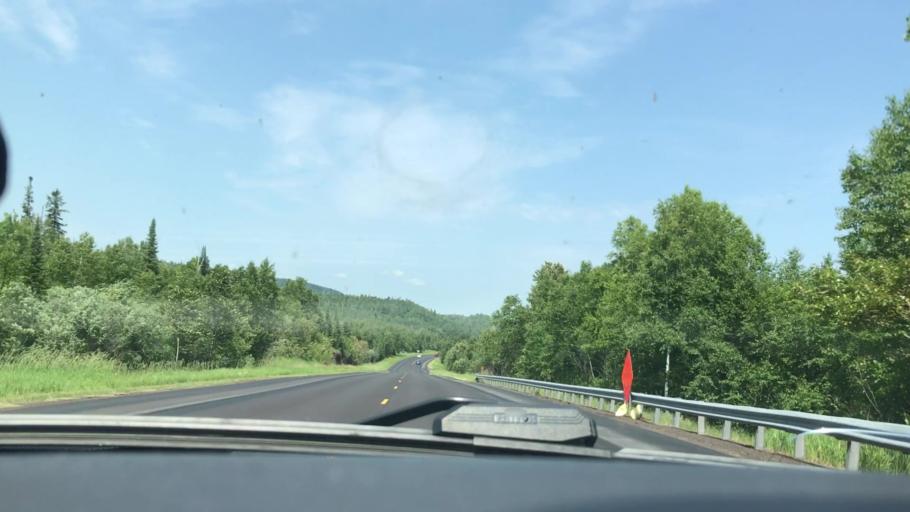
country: US
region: Minnesota
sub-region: Lake County
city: Silver Bay
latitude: 47.3508
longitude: -91.1836
